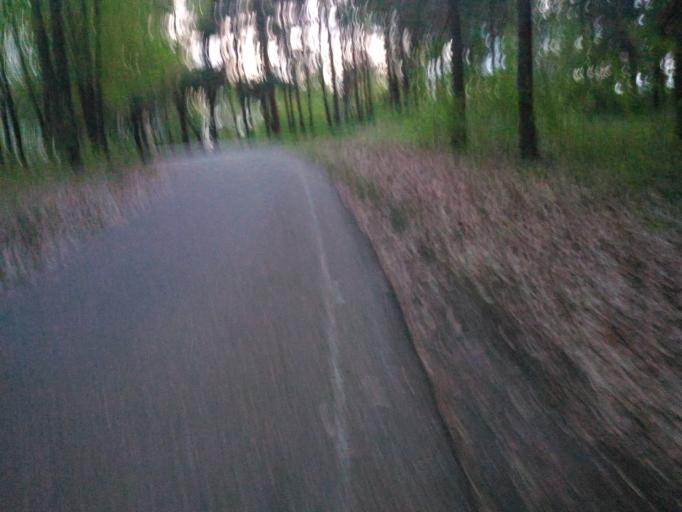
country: RU
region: Ulyanovsk
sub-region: Ulyanovskiy Rayon
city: Ulyanovsk
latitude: 54.2746
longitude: 48.3570
